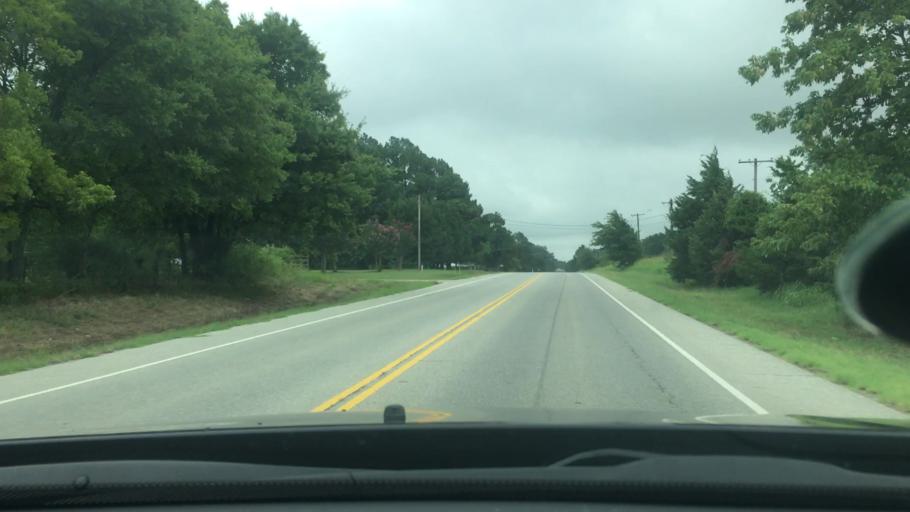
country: US
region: Oklahoma
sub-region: Bryan County
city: Colbert
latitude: 33.8530
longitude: -96.5248
